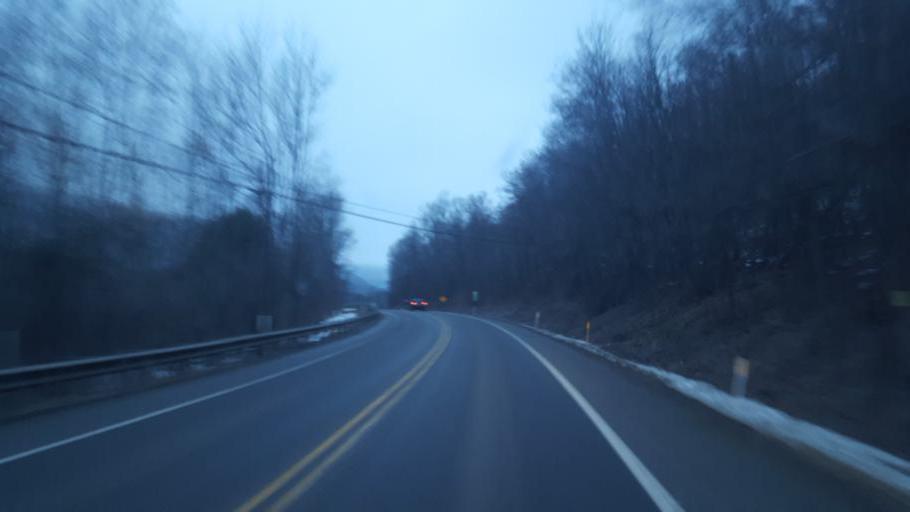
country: US
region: Pennsylvania
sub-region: Potter County
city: Coudersport
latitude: 41.7510
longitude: -78.1000
